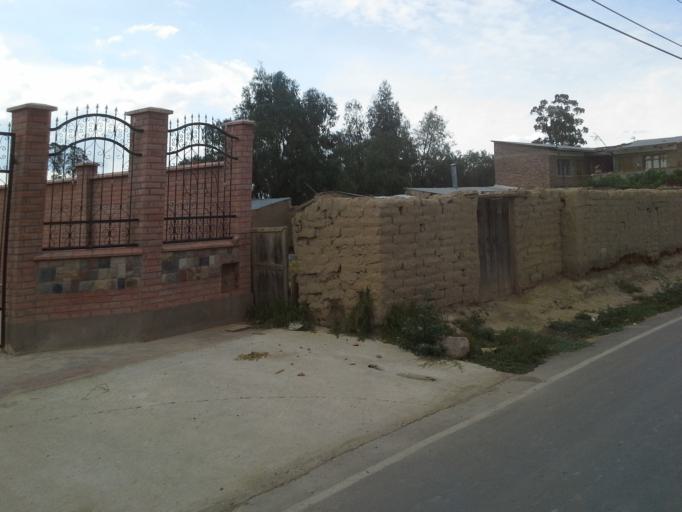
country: BO
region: Cochabamba
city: Tarata
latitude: -17.5830
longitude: -66.0163
